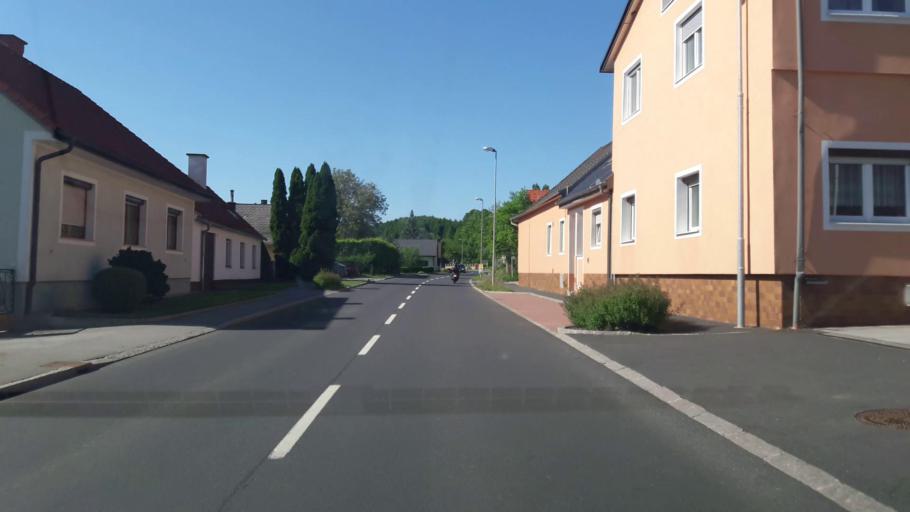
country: AT
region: Burgenland
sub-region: Politischer Bezirk Gussing
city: Ollersdorf im Burgenland
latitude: 47.1861
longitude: 16.1643
